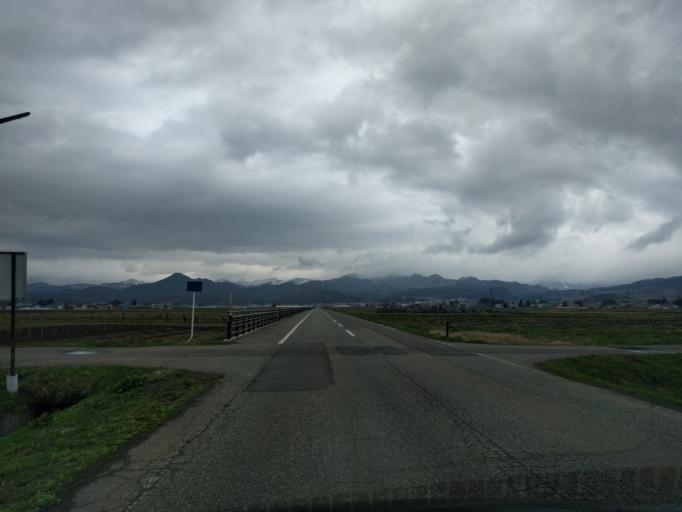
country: JP
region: Fukushima
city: Kitakata
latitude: 37.6336
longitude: 139.9134
